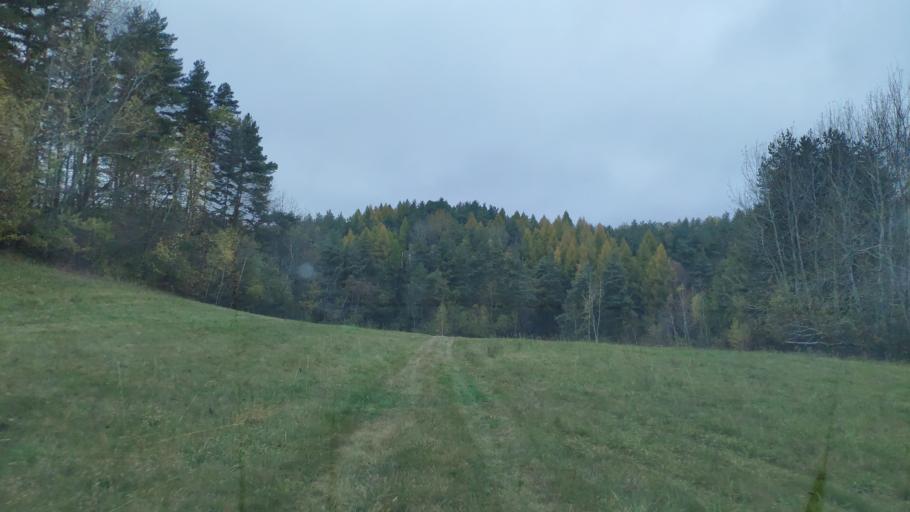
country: SK
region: Presovsky
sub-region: Okres Presov
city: Presov
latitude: 48.9331
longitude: 21.0971
